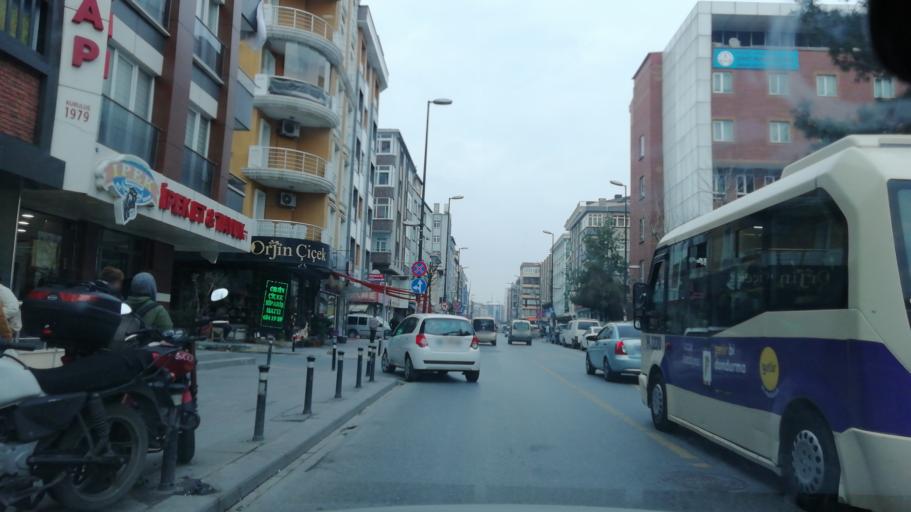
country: TR
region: Istanbul
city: Bahcelievler
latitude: 41.0077
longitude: 28.8414
